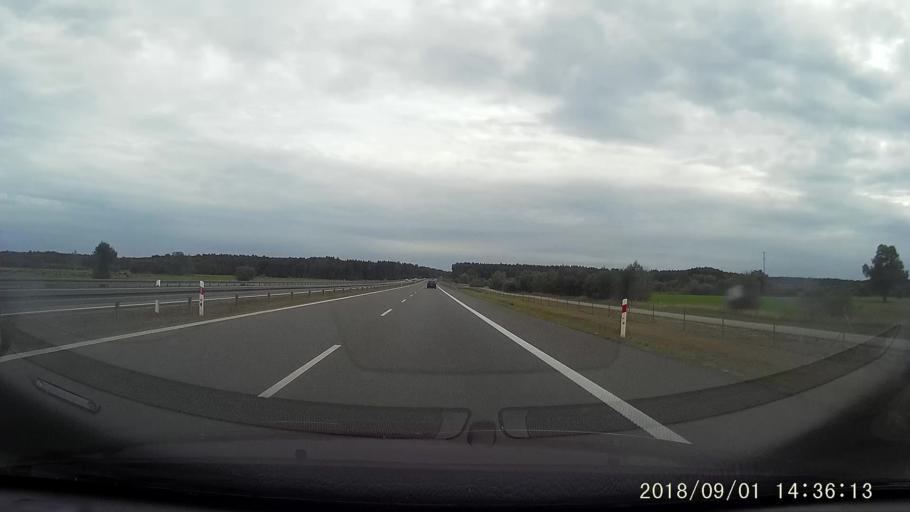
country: PL
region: West Pomeranian Voivodeship
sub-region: Powiat mysliborski
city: Nowogrodek Pomorski
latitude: 52.8669
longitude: 15.0304
